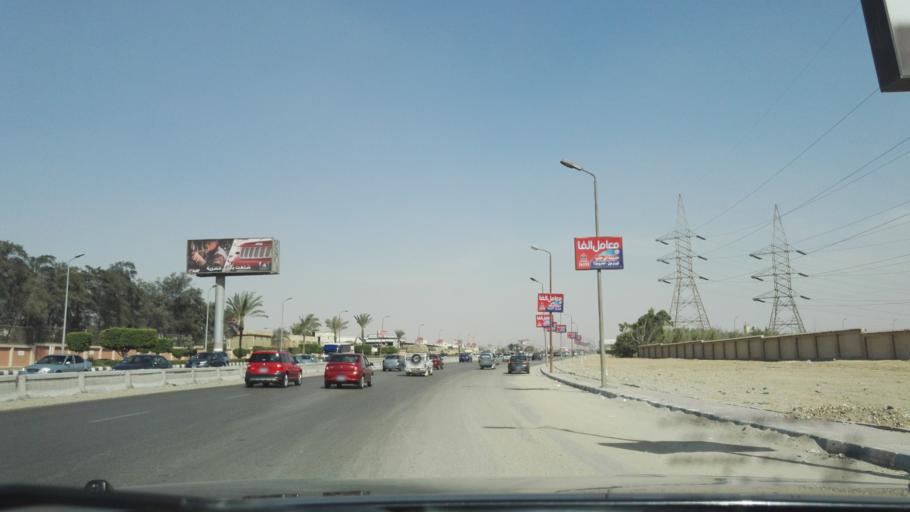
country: EG
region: Muhafazat al Qalyubiyah
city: Al Khankah
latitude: 30.0815
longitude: 31.4109
